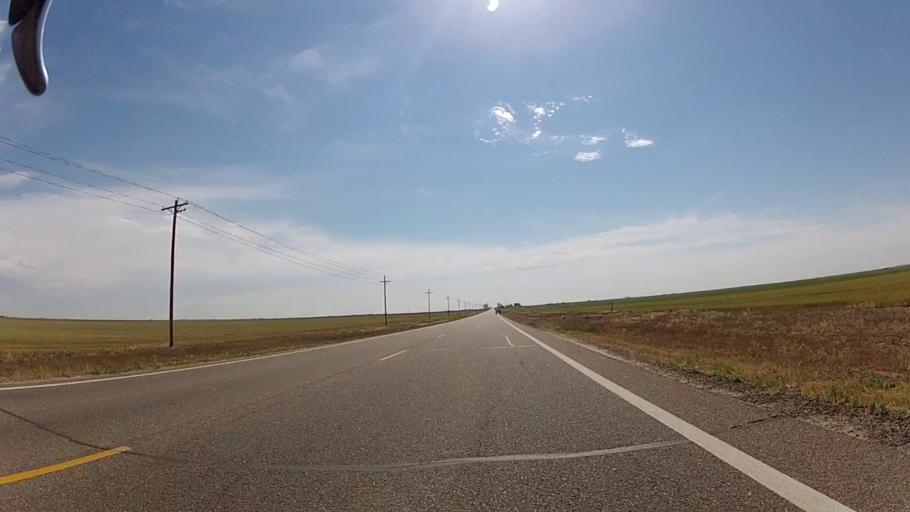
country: US
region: Kansas
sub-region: Grant County
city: Ulysses
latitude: 37.5617
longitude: -101.2814
